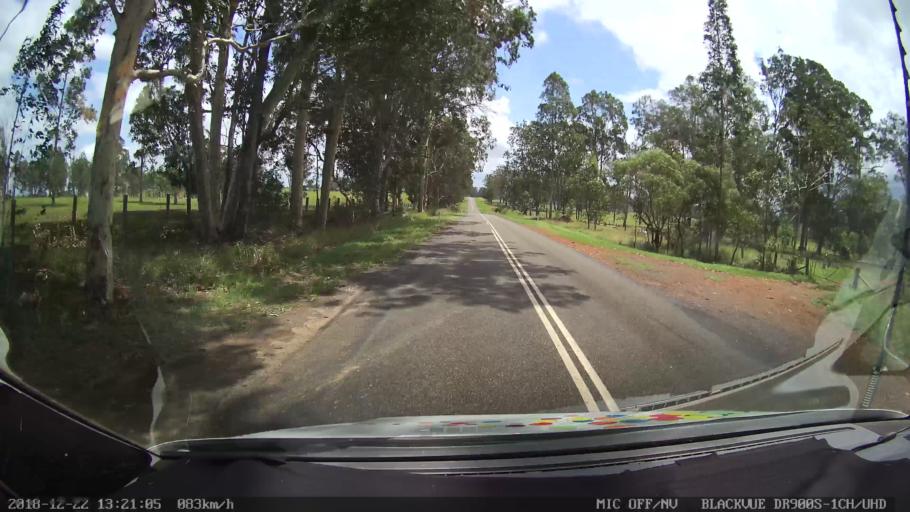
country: AU
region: New South Wales
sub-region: Clarence Valley
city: Coutts Crossing
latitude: -29.7734
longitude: 152.9235
